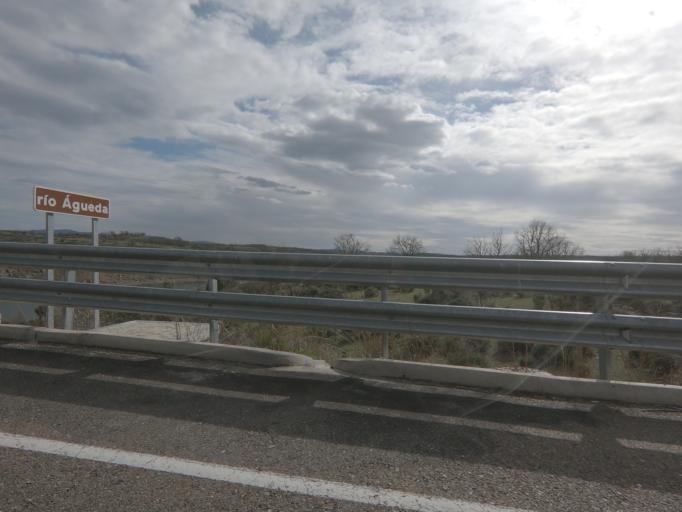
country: ES
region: Castille and Leon
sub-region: Provincia de Salamanca
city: Robleda
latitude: 40.4308
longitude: -6.6035
